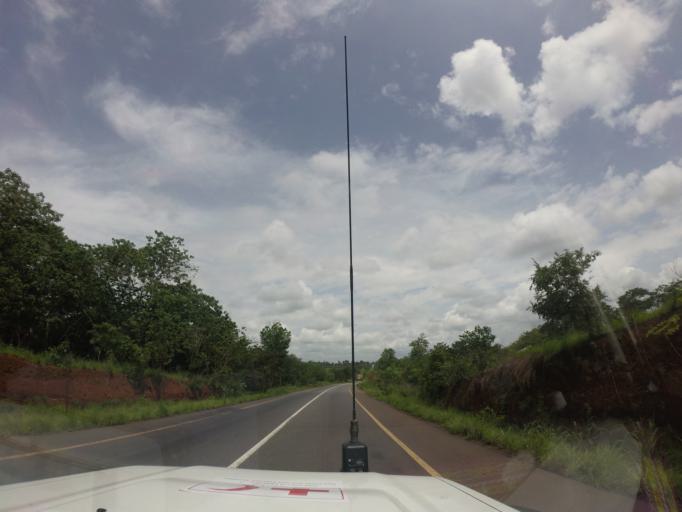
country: SL
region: Northern Province
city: Port Loko
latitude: 8.7677
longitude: -12.7726
